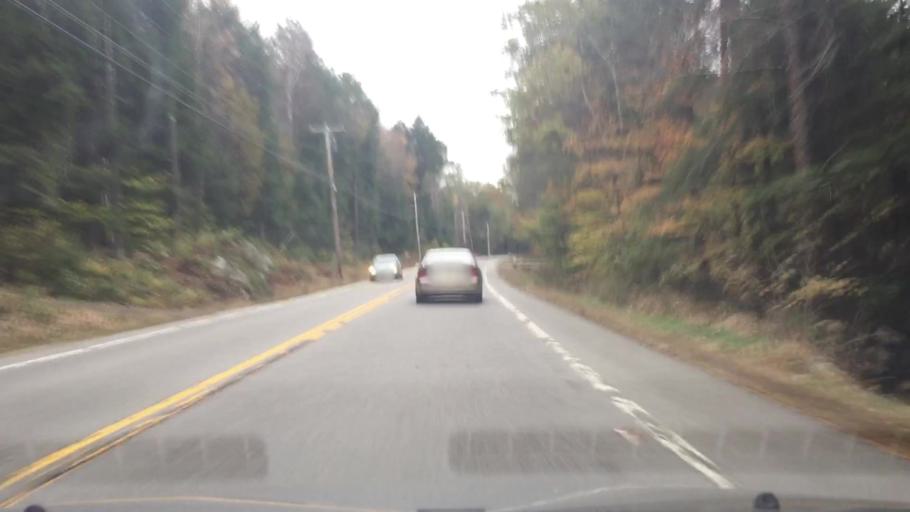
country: US
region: New Hampshire
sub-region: Cheshire County
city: Keene
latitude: 43.0098
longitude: -72.2621
